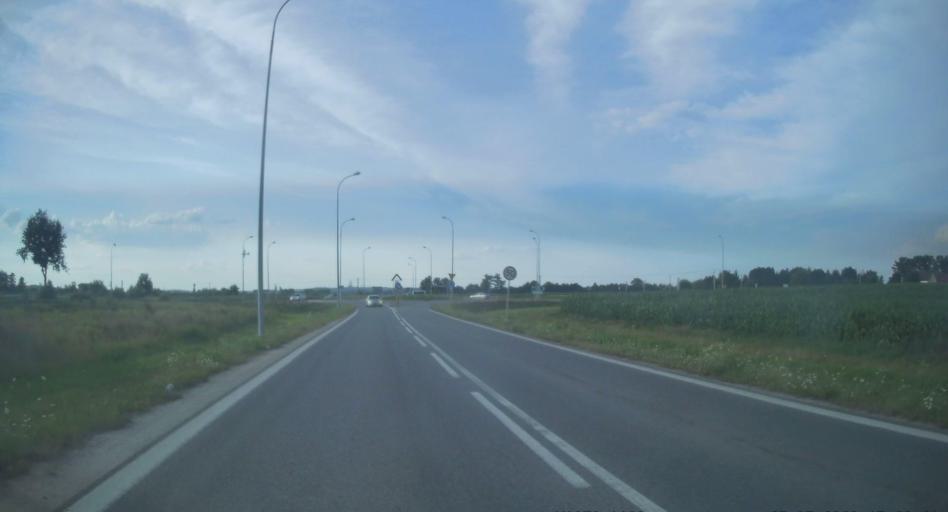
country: PL
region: Lesser Poland Voivodeship
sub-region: Powiat brzeski
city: Szczurowa
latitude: 50.1218
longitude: 20.6130
